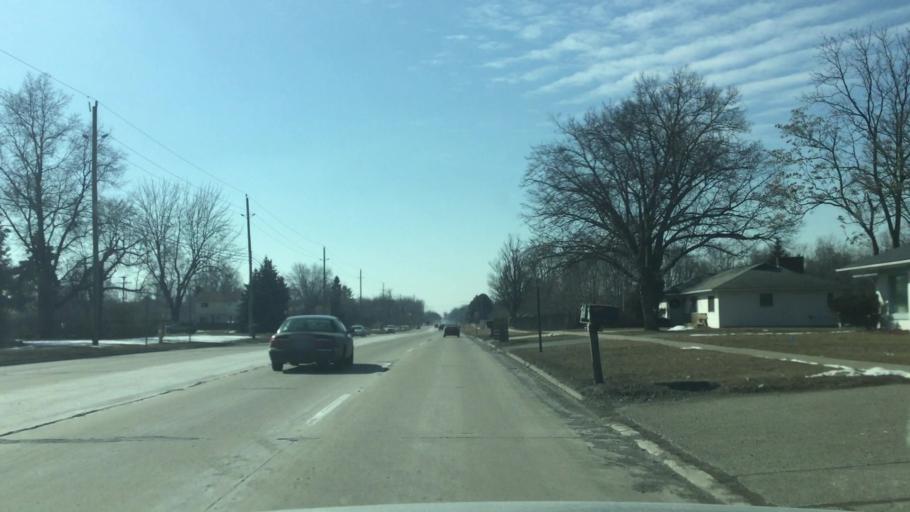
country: US
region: Michigan
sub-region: Wayne County
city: Westland
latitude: 42.3099
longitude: -83.3950
